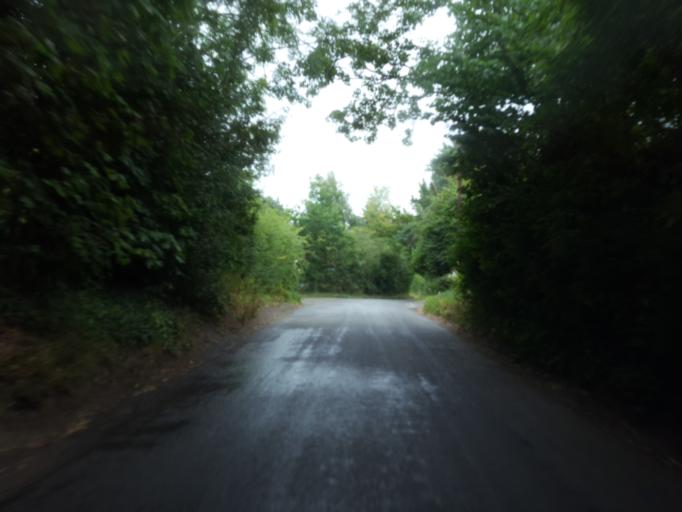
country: GB
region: England
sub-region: Kent
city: Marden
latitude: 51.2187
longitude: 0.4759
